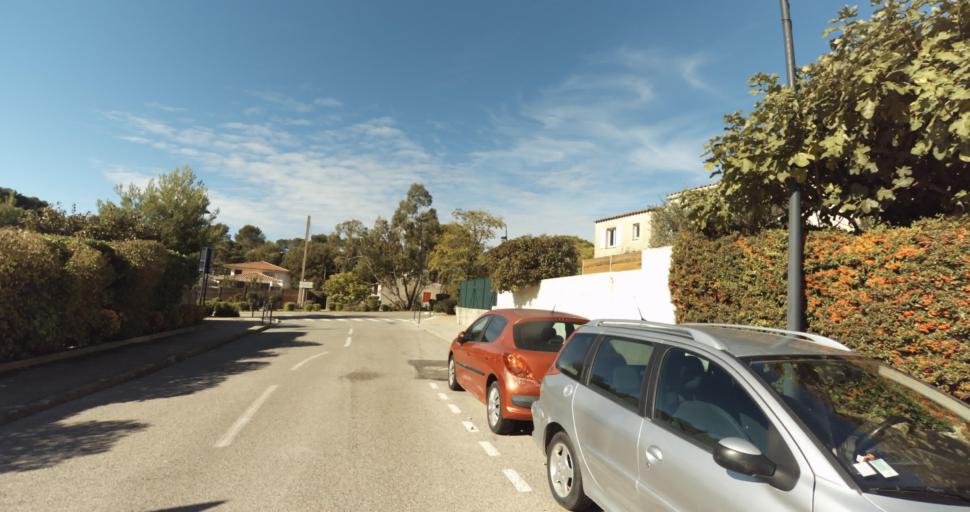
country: FR
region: Provence-Alpes-Cote d'Azur
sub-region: Departement des Bouches-du-Rhone
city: Venelles
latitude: 43.5960
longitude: 5.4765
